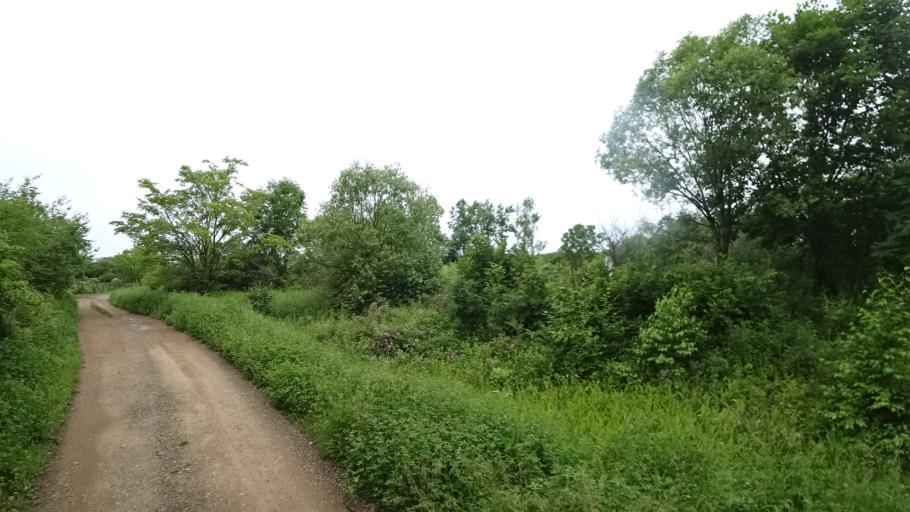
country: RU
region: Primorskiy
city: Novosysoyevka
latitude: 44.2099
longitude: 133.3280
